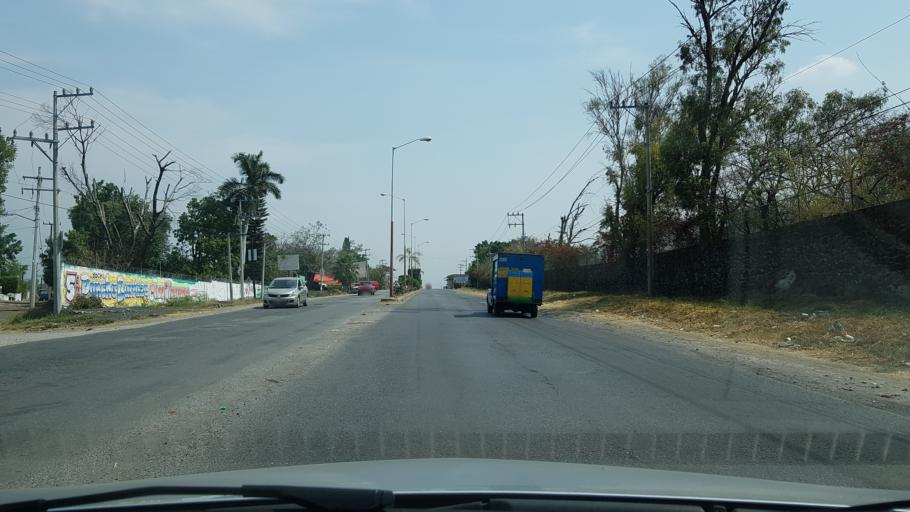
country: MX
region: Morelos
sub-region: Xochitepec
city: Chiconcuac
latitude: 18.7922
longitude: -99.2023
